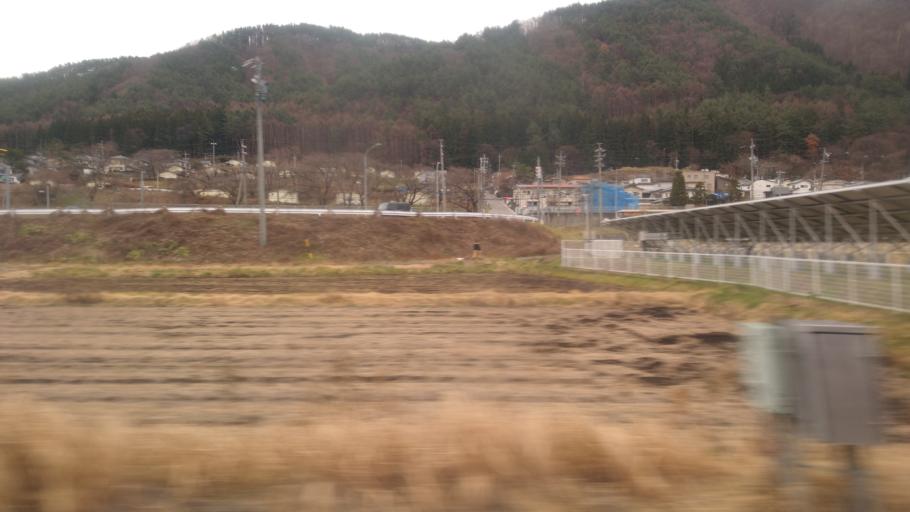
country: JP
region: Nagano
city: Shiojiri
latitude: 36.0749
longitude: 137.9062
